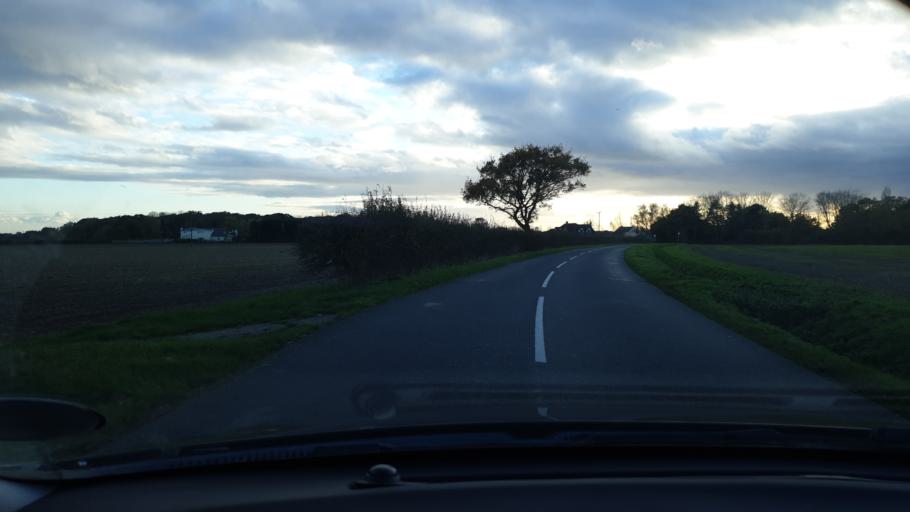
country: GB
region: England
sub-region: Essex
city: Mistley
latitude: 51.9011
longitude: 1.1431
